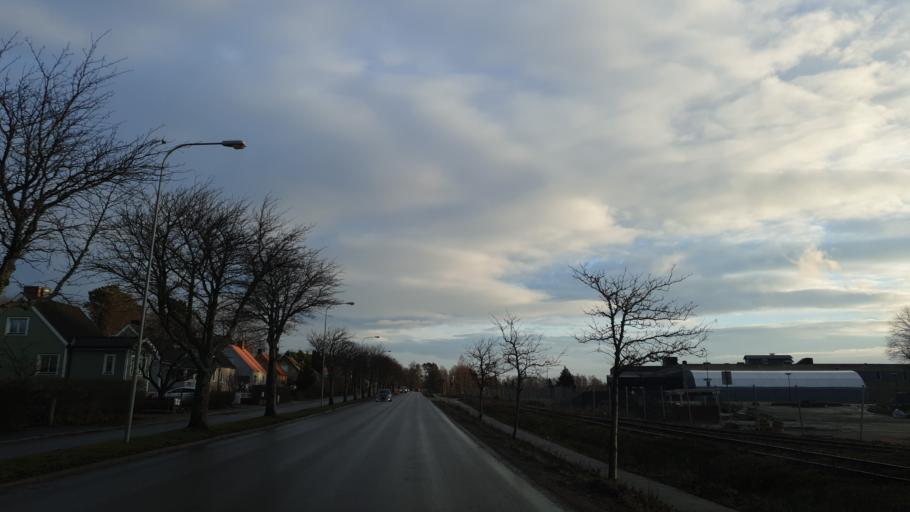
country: SE
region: Gaevleborg
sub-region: Hudiksvalls Kommun
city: Hudiksvall
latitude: 61.7246
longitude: 17.1340
